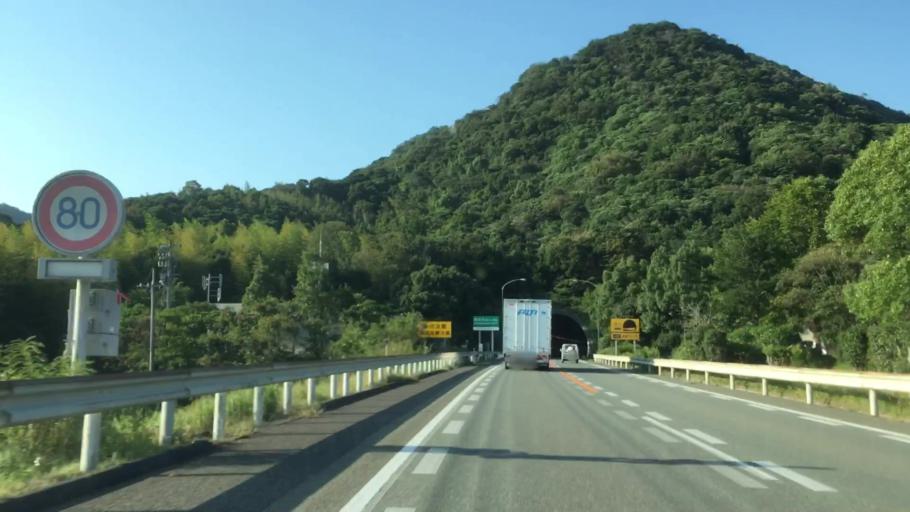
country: JP
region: Yamaguchi
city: Ogori-shimogo
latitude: 34.0995
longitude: 131.4513
